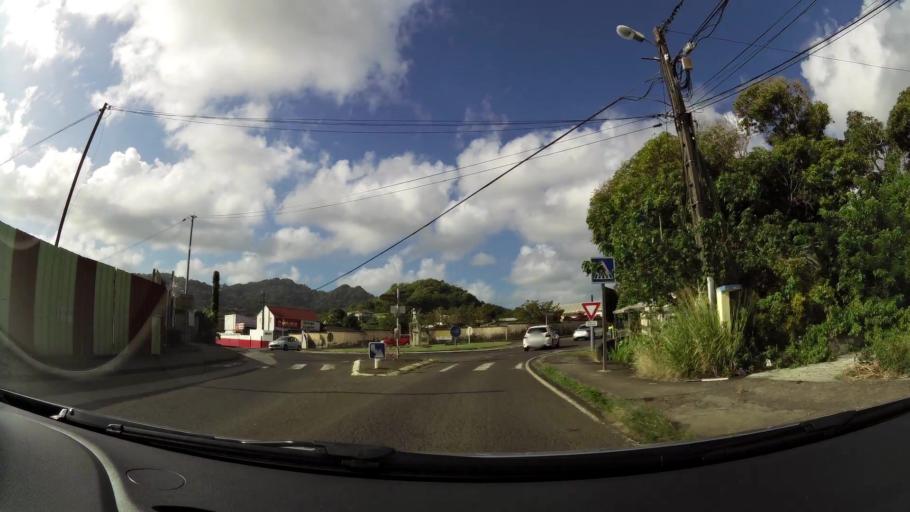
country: MQ
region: Martinique
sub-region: Martinique
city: Le Robert
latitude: 14.6737
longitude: -60.9431
